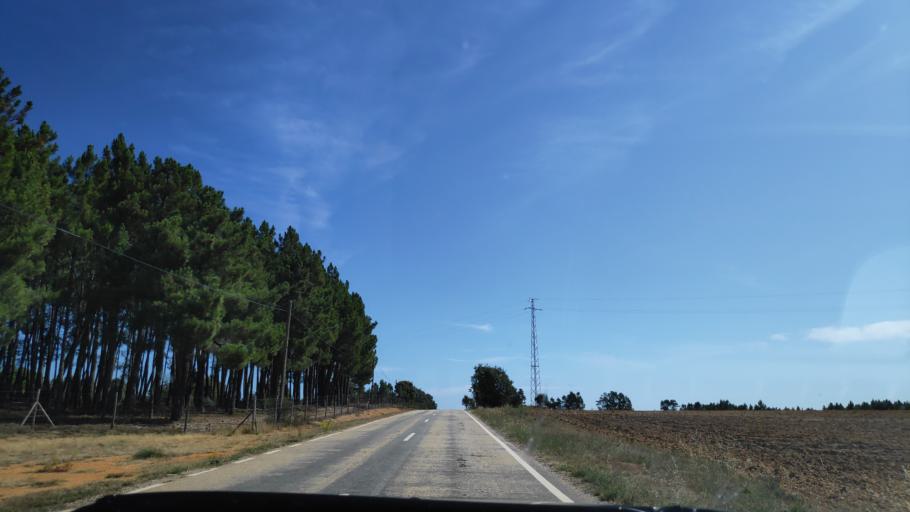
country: ES
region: Castille and Leon
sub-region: Provincia de Zamora
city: Alcanices
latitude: 41.5955
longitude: -6.3504
